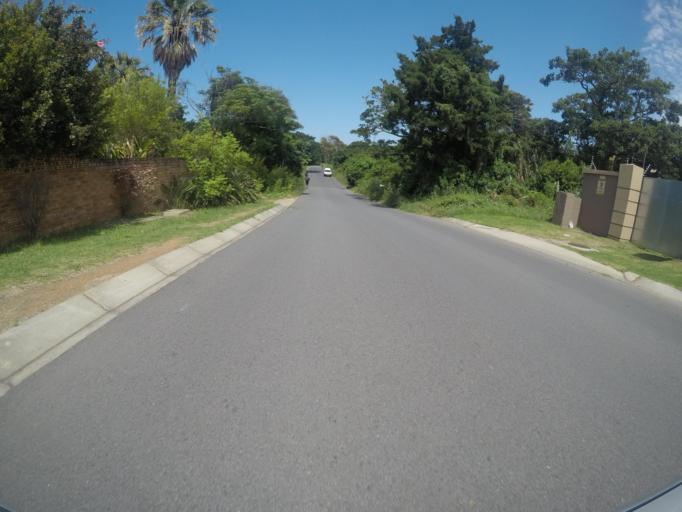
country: ZA
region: Eastern Cape
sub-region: Buffalo City Metropolitan Municipality
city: East London
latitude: -32.9488
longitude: 28.0029
